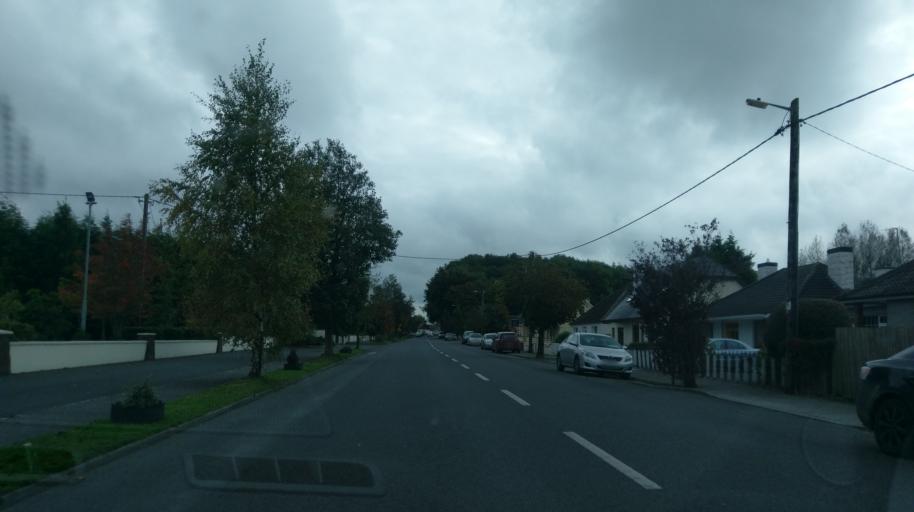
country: IE
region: Connaught
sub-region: County Galway
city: Loughrea
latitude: 53.4692
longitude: -8.4976
